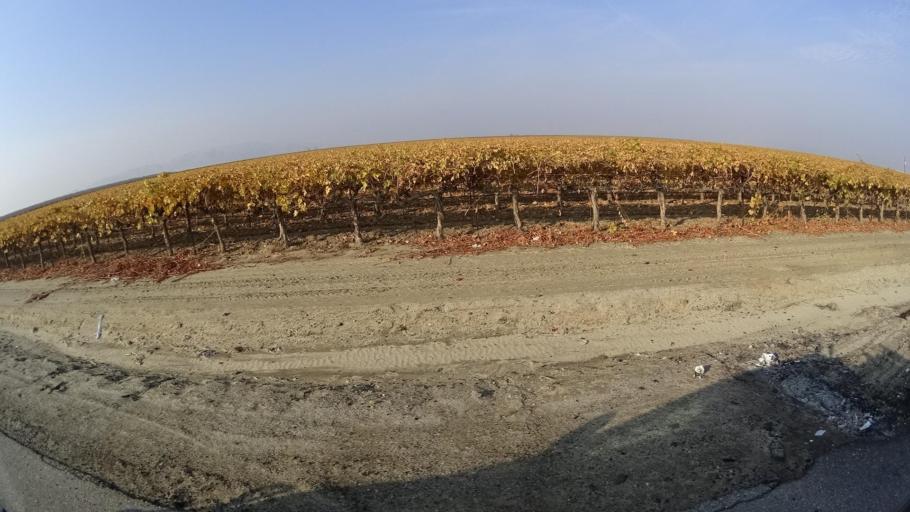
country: US
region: California
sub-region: Kern County
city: Arvin
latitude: 35.0506
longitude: -118.9176
